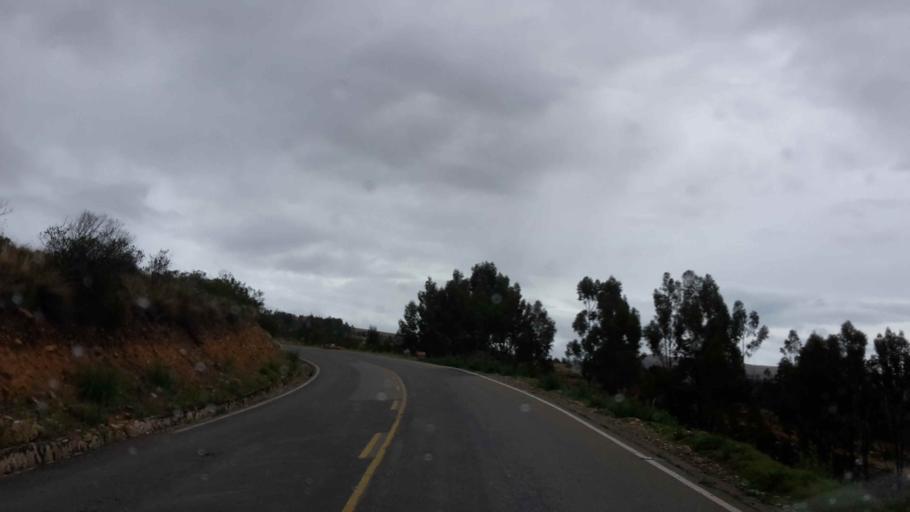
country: BO
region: Cochabamba
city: Arani
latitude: -17.4631
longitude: -65.6867
